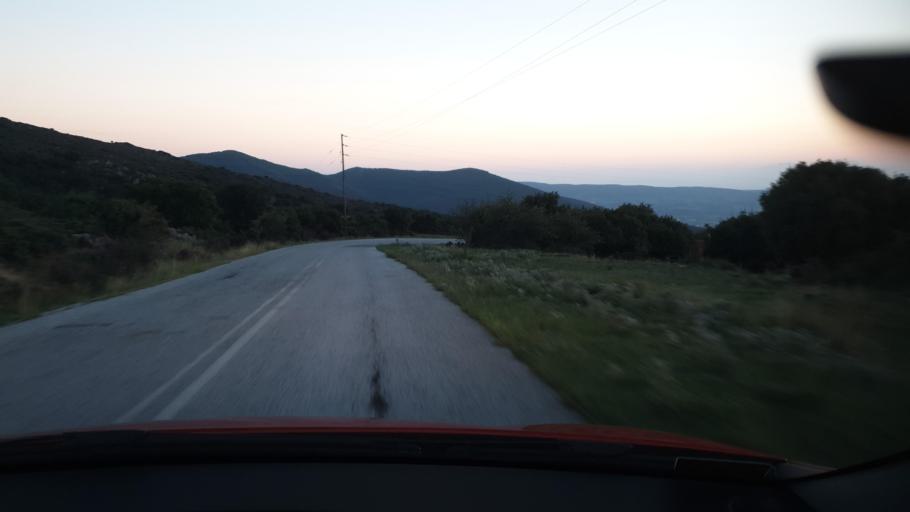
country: GR
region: Central Macedonia
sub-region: Nomos Thessalonikis
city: Peristera
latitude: 40.5181
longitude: 23.1871
